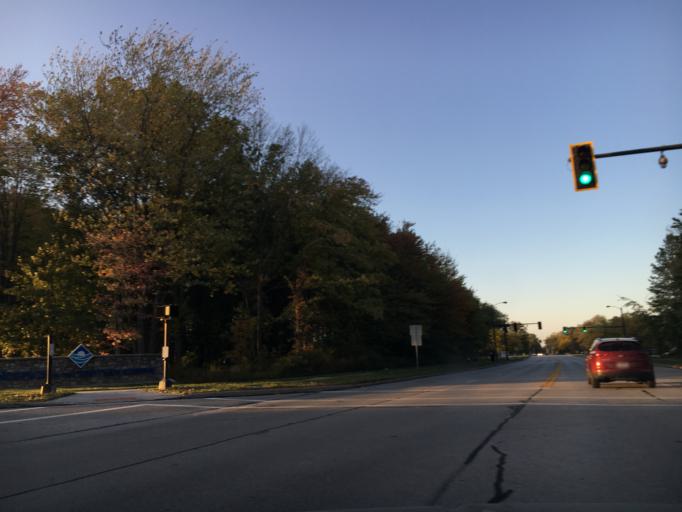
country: US
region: Ohio
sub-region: Cuyahoga County
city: Bay Village
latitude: 41.4719
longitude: -81.9506
